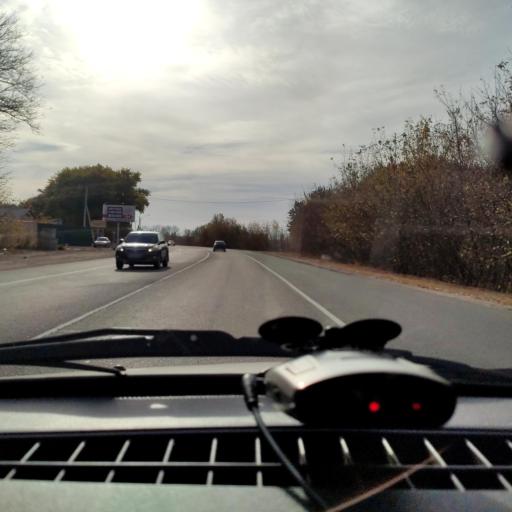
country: RU
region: Voronezj
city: Devitsa
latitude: 51.5992
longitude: 38.9730
